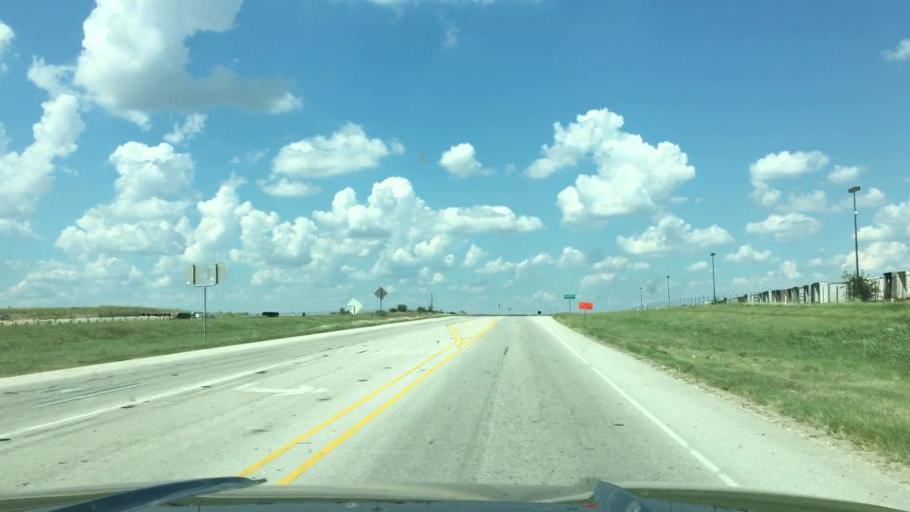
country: US
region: Texas
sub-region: Tarrant County
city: Haslet
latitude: 32.9905
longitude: -97.3423
